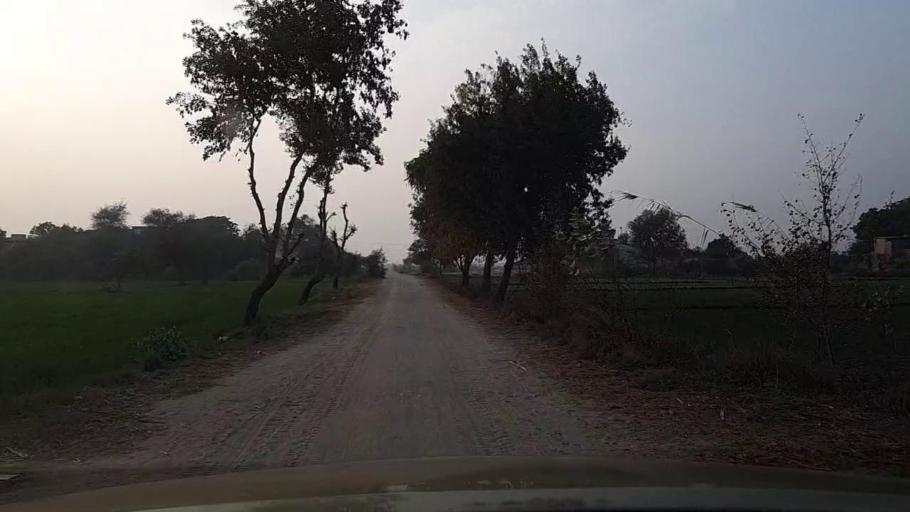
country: PK
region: Sindh
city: Sanghar
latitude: 26.1857
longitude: 68.9679
